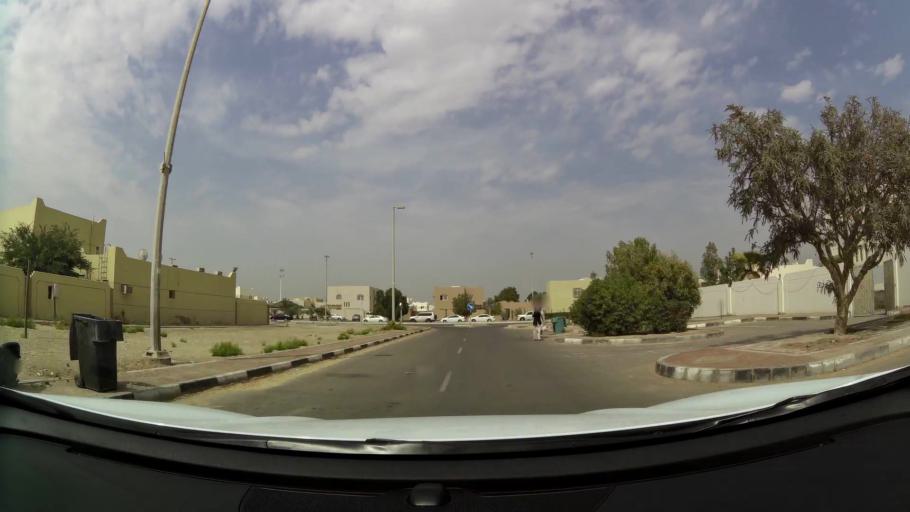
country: AE
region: Abu Dhabi
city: Abu Dhabi
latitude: 24.3123
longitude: 54.6340
